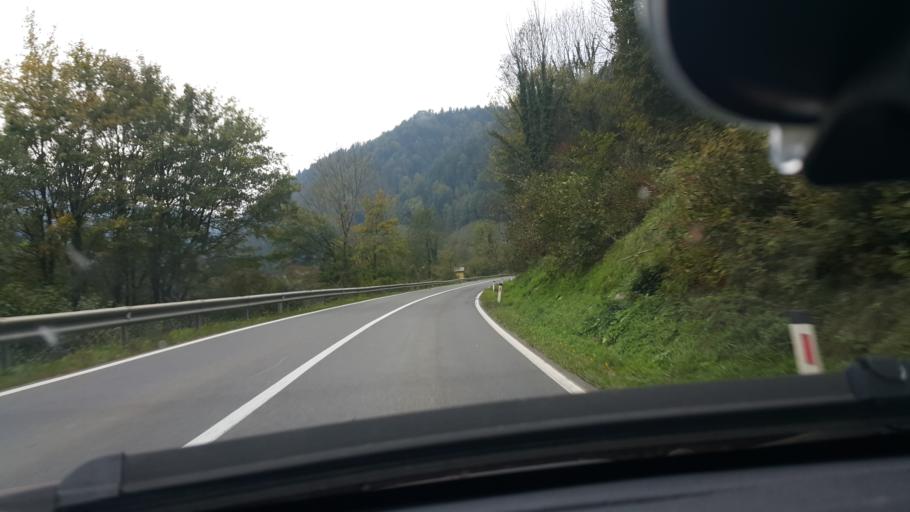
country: SI
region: Podvelka
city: Podvelka
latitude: 46.5892
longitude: 15.2969
